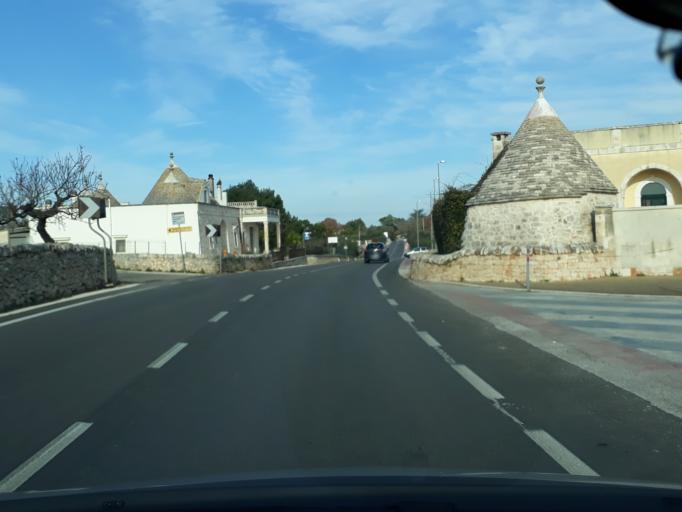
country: IT
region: Apulia
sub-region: Provincia di Bari
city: Locorotondo
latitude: 40.7751
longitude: 17.3357
